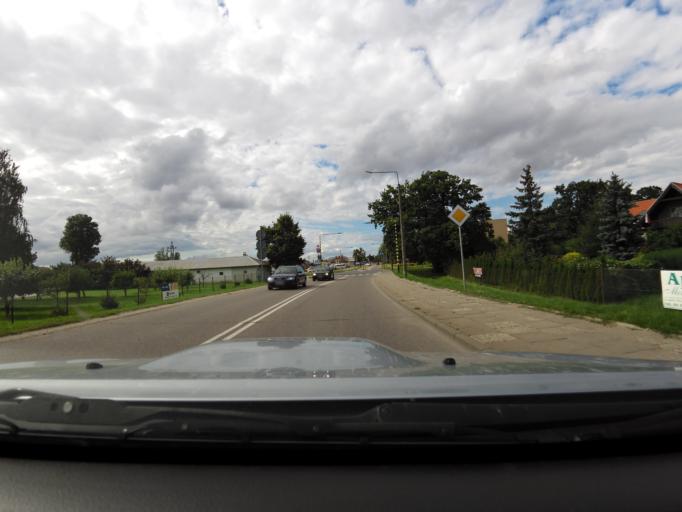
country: PL
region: Pomeranian Voivodeship
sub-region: Powiat nowodworski
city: Nowy Dwor Gdanski
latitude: 54.2085
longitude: 19.1134
